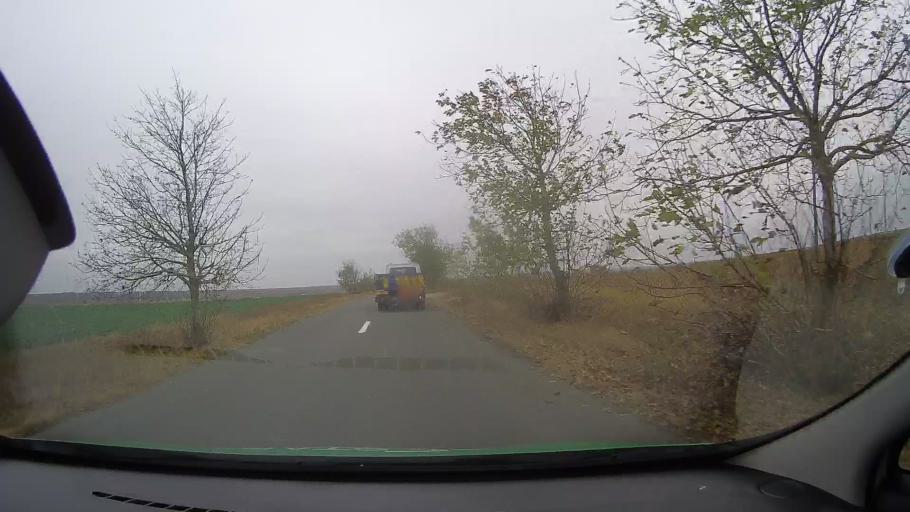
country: RO
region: Constanta
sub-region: Comuna Targusor
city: Targusor
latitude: 44.4806
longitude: 28.3733
